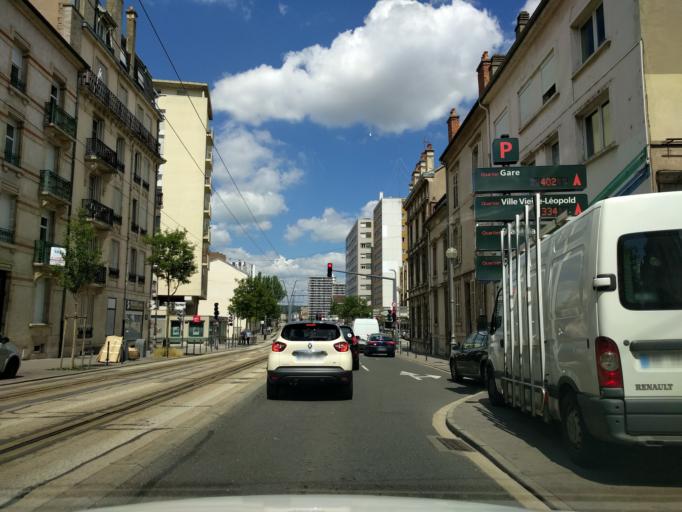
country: FR
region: Lorraine
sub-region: Departement de Meurthe-et-Moselle
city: Nancy
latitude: 48.6835
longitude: 6.1771
